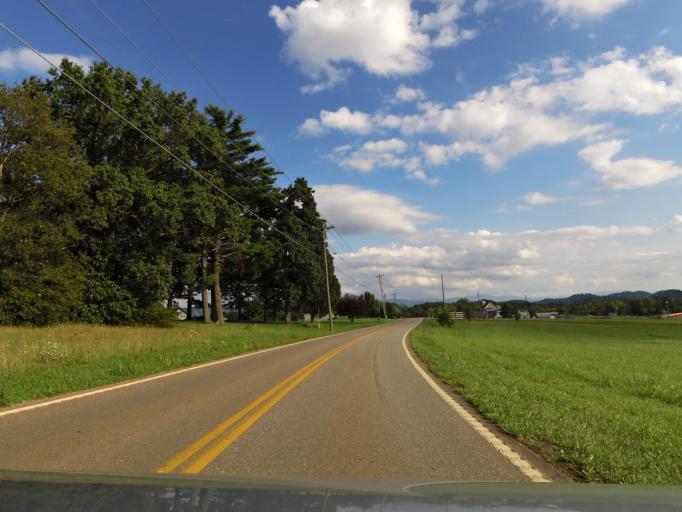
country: US
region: Tennessee
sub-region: Loudon County
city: Greenback
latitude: 35.6418
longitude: -84.1008
